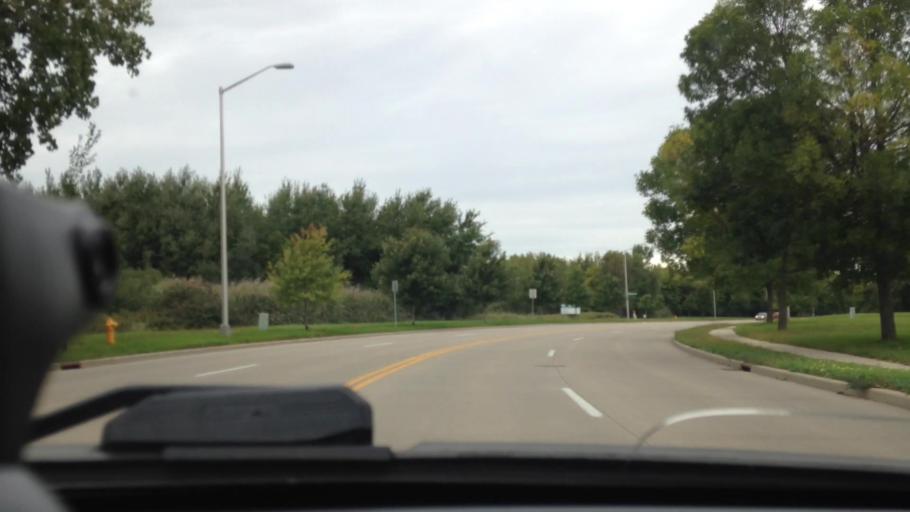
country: US
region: Wisconsin
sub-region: Fond du Lac County
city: North Fond du Lac
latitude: 43.7932
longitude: -88.4752
